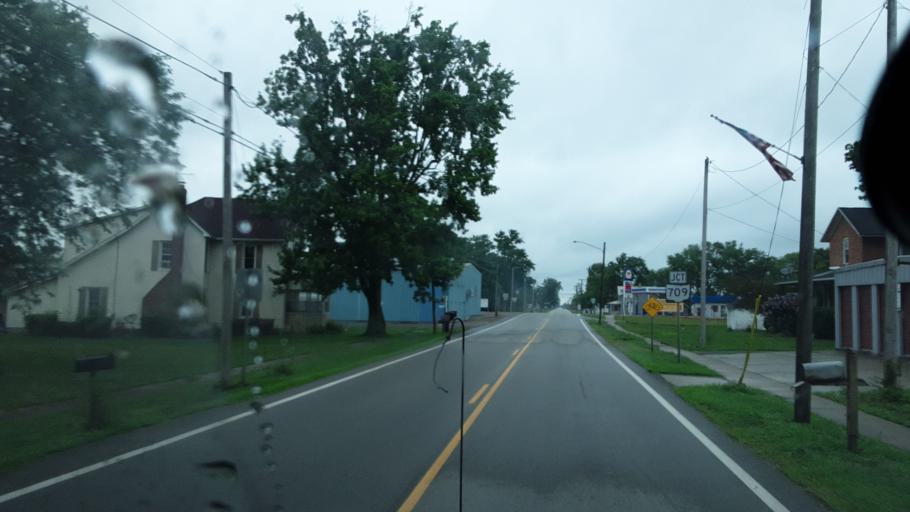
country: US
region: Ohio
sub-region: Mercer County
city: Rockford
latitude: 40.7702
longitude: -84.6224
